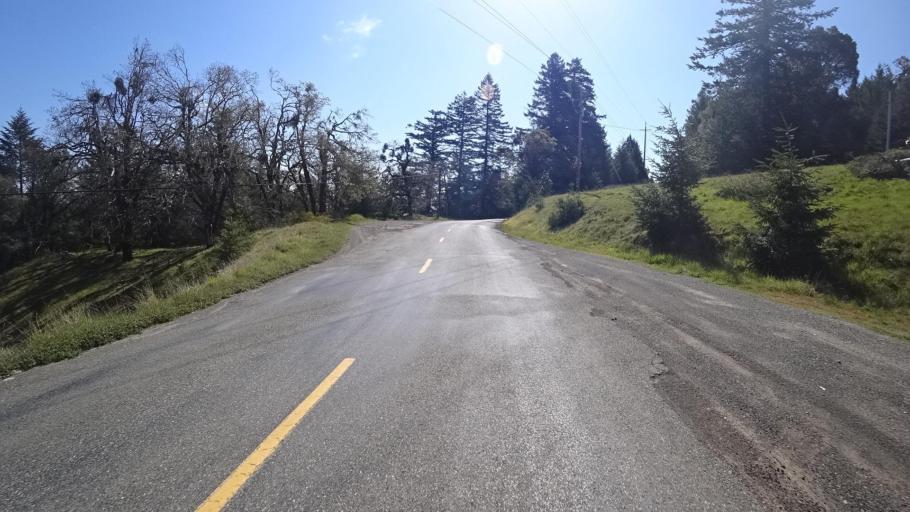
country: US
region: California
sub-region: Humboldt County
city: Redway
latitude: 40.0951
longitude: -123.6809
